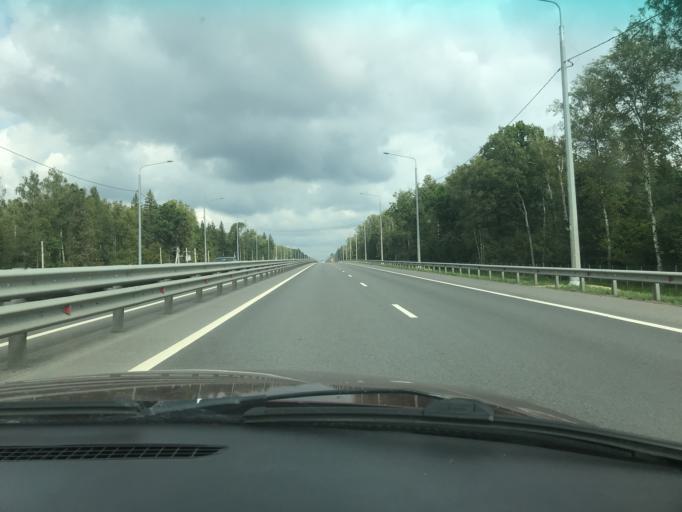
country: RU
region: Kaluga
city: Mstikhino
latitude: 54.6481
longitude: 36.1362
